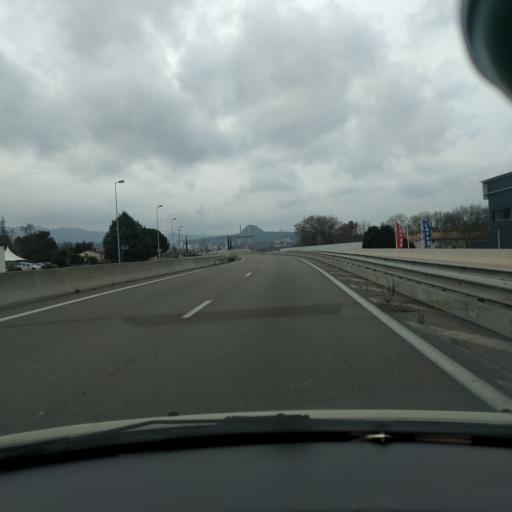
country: FR
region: Provence-Alpes-Cote d'Azur
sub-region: Departement des Bouches-du-Rhone
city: Gardanne
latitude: 43.4676
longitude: 5.4675
